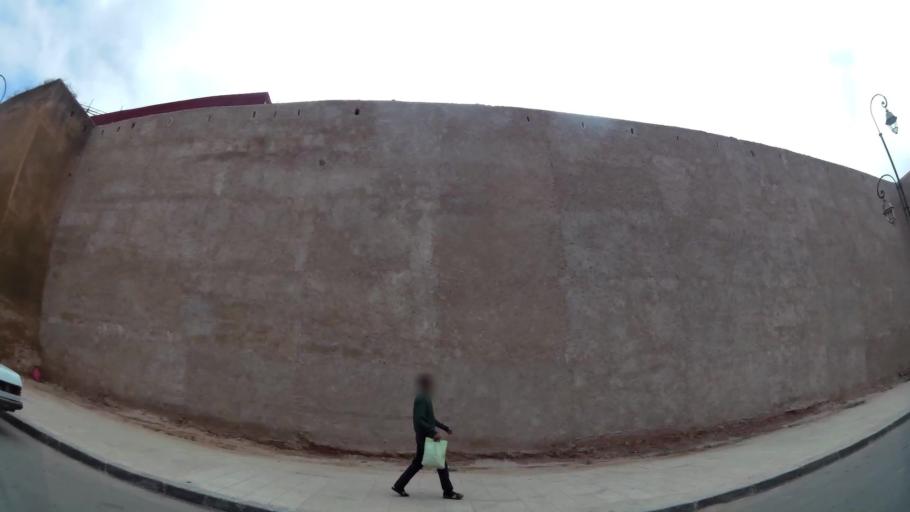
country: MA
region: Rabat-Sale-Zemmour-Zaer
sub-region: Rabat
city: Rabat
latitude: 34.0243
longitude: -6.8412
